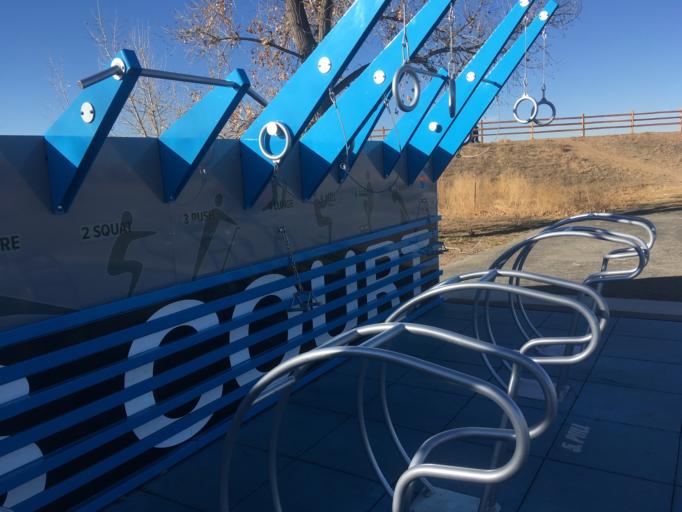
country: US
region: Colorado
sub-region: Weld County
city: Firestone
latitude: 40.1186
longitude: -104.9447
